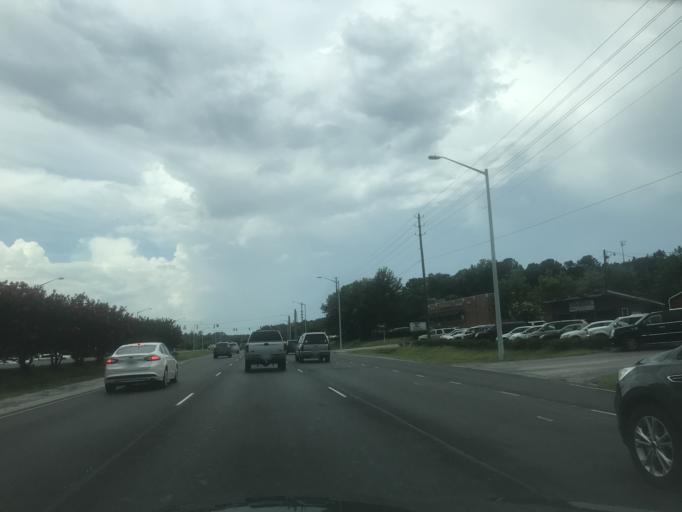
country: US
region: North Carolina
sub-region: Johnston County
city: Clayton
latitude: 35.6492
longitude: -78.4682
